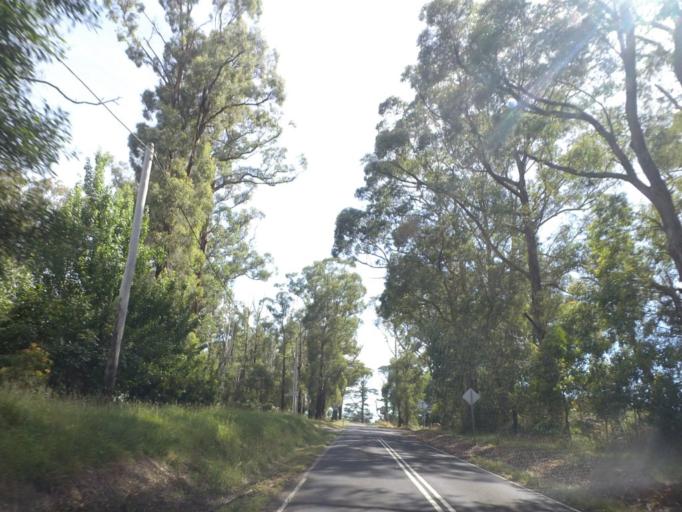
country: AU
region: Victoria
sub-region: Nillumbik
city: Saint Andrews
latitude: -37.5377
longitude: 145.3395
